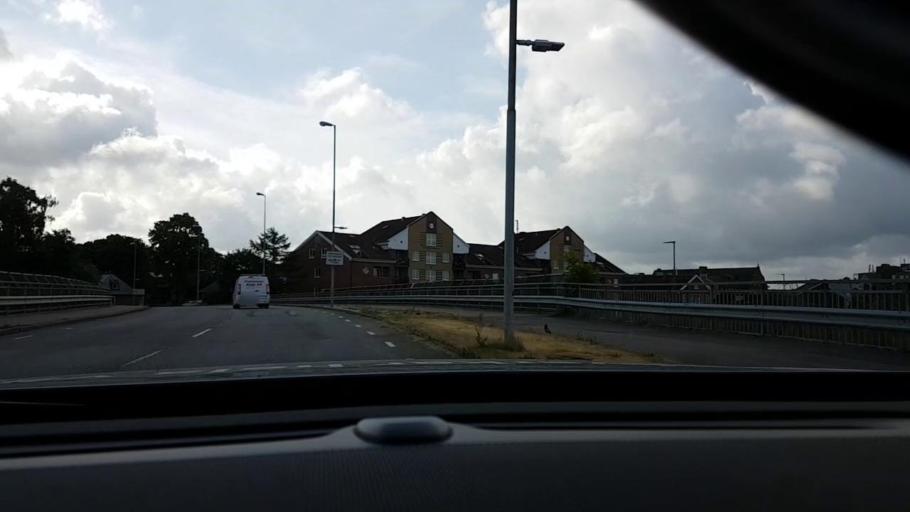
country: SE
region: Skane
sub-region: Hassleholms Kommun
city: Hassleholm
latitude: 56.1608
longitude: 13.7643
